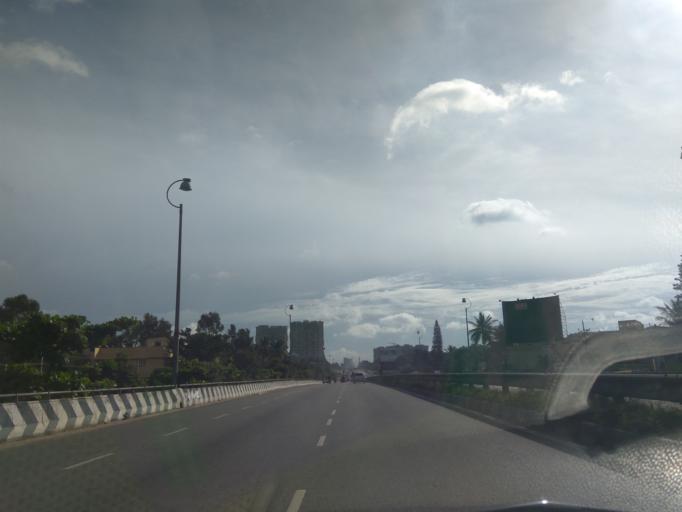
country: IN
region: Karnataka
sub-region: Bangalore Rural
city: Hoskote
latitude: 13.0361
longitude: 77.7363
